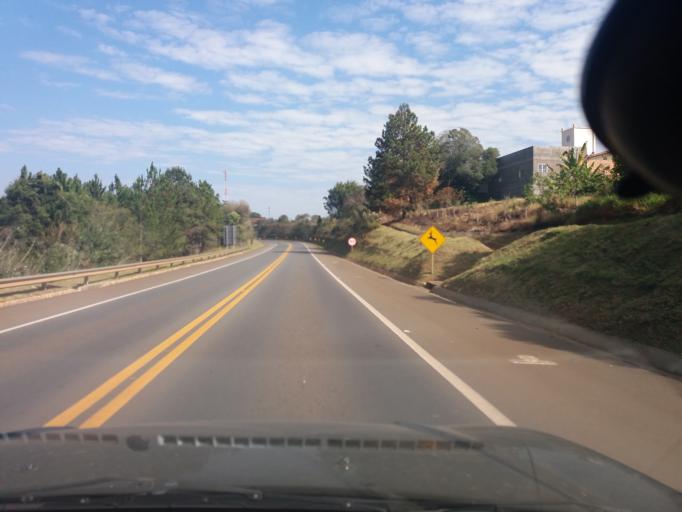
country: BR
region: Sao Paulo
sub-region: Buri
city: Buri
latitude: -23.9256
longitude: -48.6922
